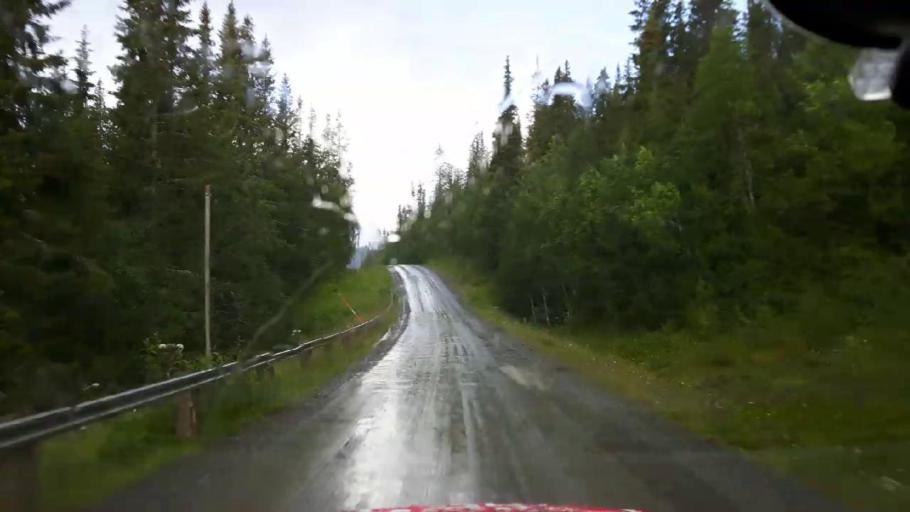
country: NO
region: Nordland
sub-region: Hattfjelldal
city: Hattfjelldal
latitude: 64.8641
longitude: 14.9175
